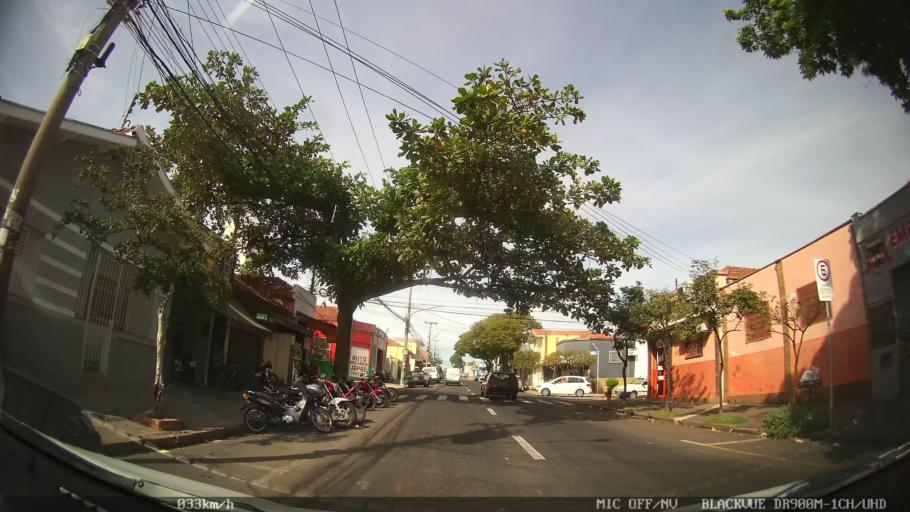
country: BR
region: Sao Paulo
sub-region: Piracicaba
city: Piracicaba
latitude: -22.7482
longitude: -47.6499
